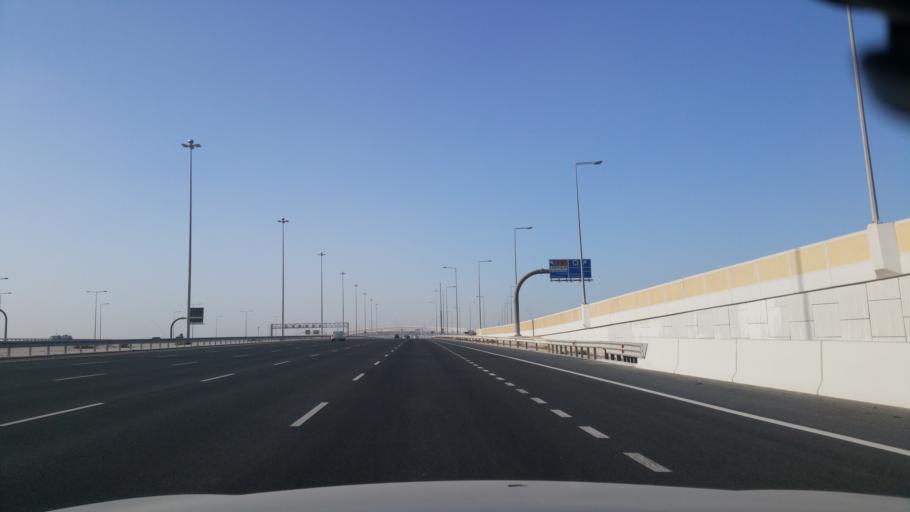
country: QA
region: Al Wakrah
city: Al Wukayr
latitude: 25.1889
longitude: 51.5464
